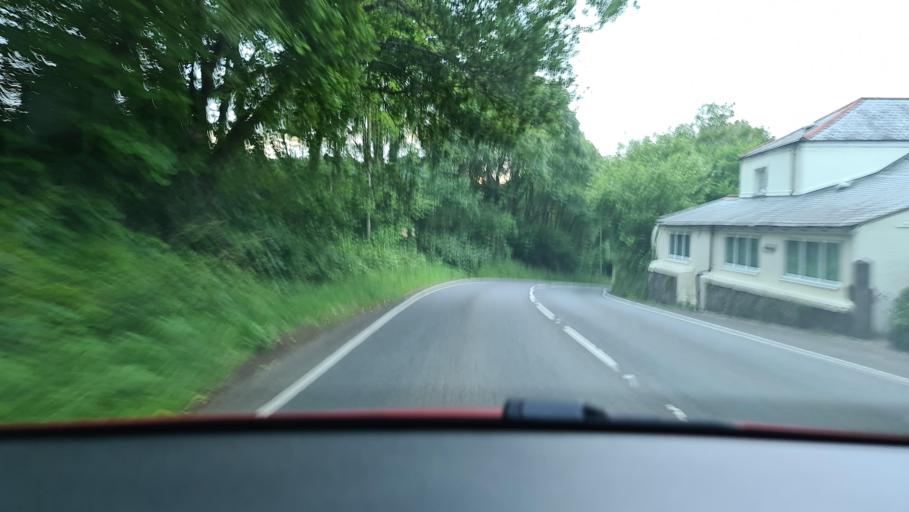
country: GB
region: England
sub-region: Cornwall
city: Looe
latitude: 50.3919
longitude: -4.3780
